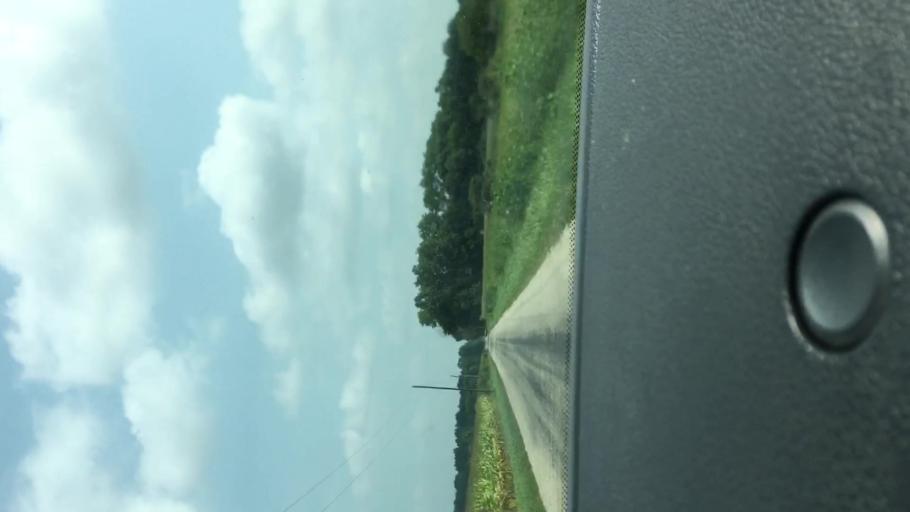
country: US
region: Indiana
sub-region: Jay County
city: Portland
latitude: 40.3969
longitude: -84.9168
